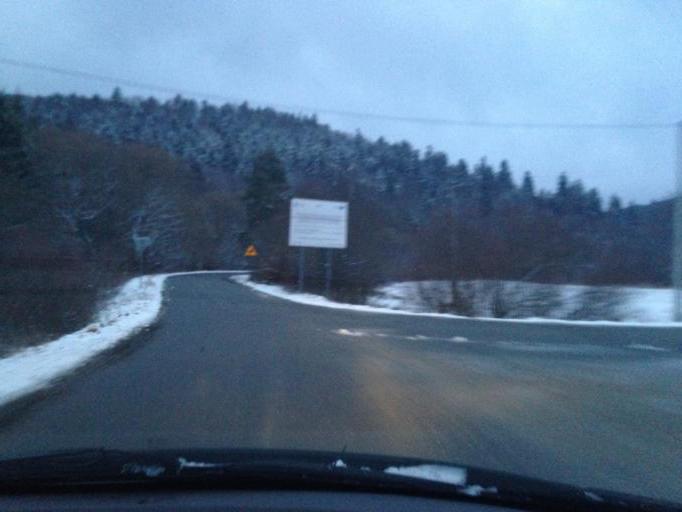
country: PL
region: Subcarpathian Voivodeship
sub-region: Powiat jasielski
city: Krempna
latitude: 49.5047
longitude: 21.5363
